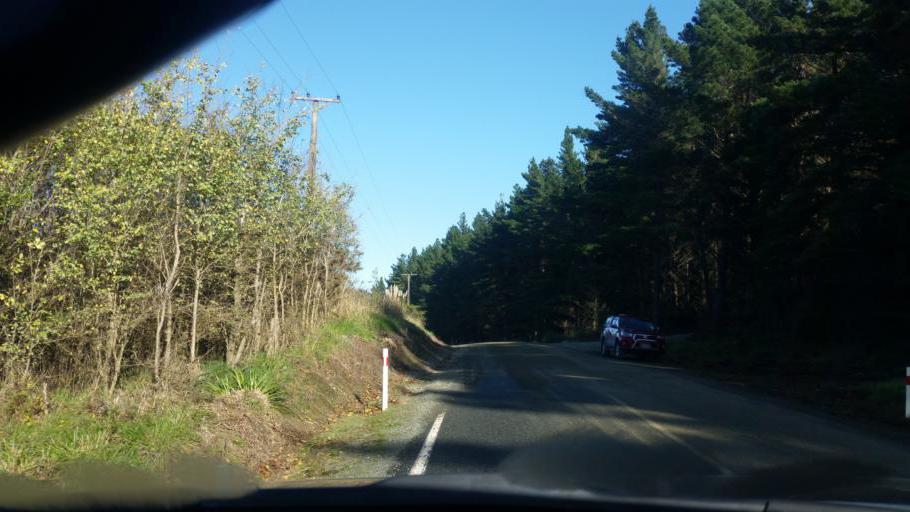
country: NZ
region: Auckland
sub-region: Auckland
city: Wellsford
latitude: -36.2302
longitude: 174.4455
